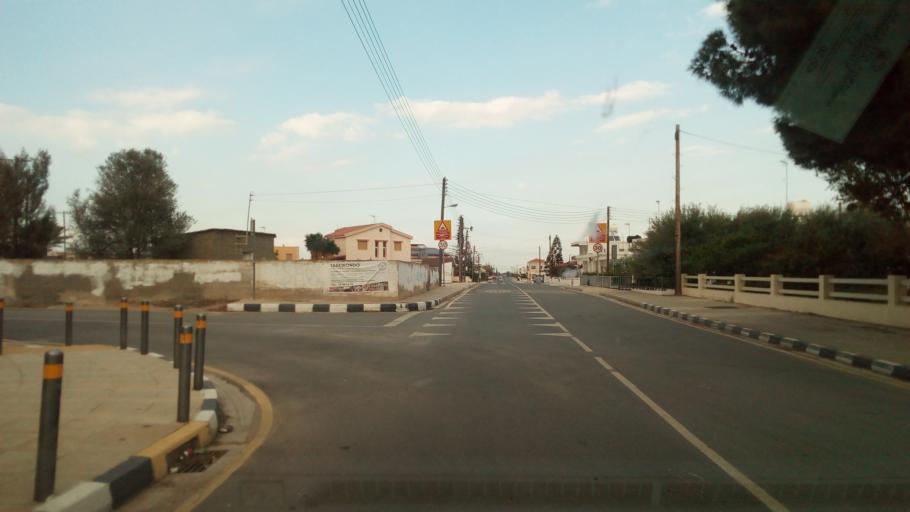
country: CY
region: Larnaka
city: Xylotymbou
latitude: 35.0194
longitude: 33.7453
